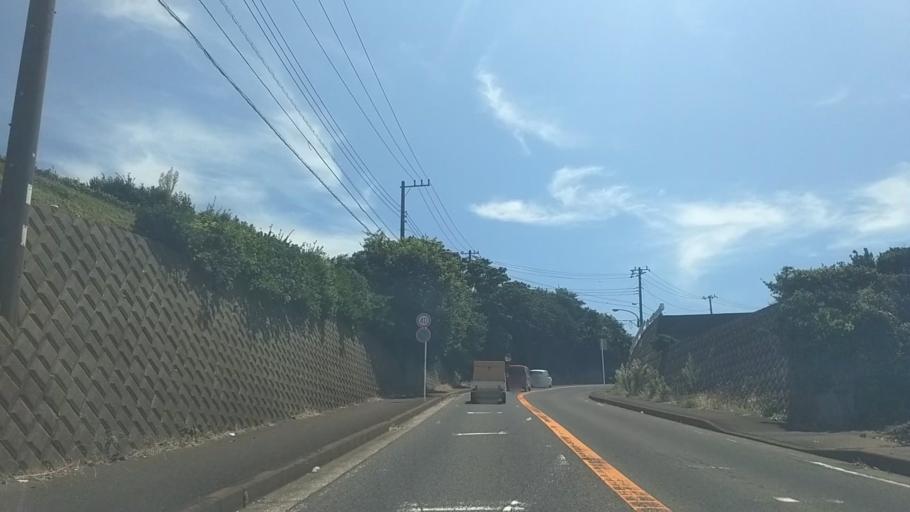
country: JP
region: Kanagawa
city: Miura
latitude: 35.1558
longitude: 139.6709
